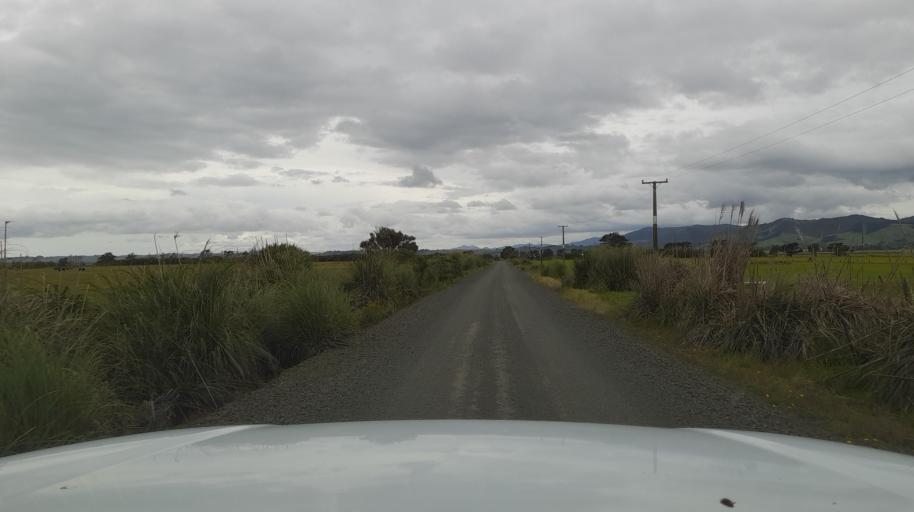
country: NZ
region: Northland
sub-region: Far North District
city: Ahipara
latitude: -35.1331
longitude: 173.1873
